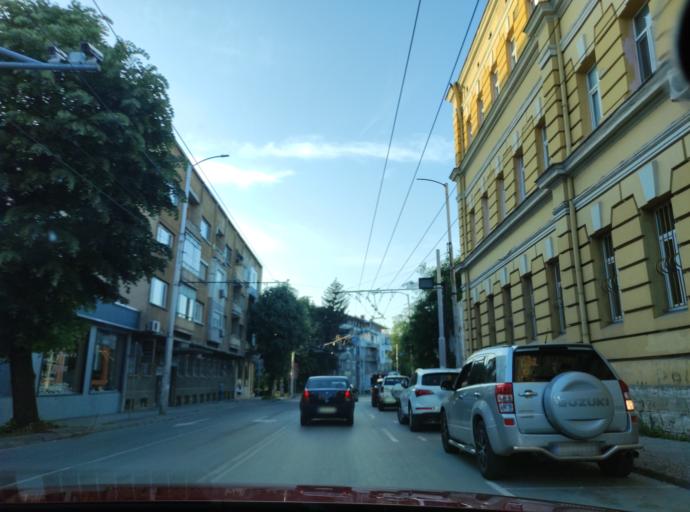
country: BG
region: Pleven
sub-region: Obshtina Pleven
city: Pleven
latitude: 43.4110
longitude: 24.6193
